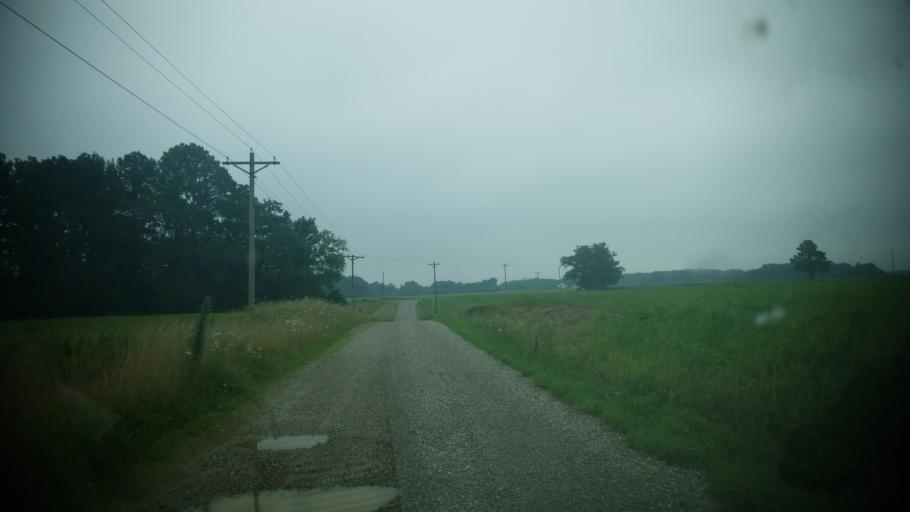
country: US
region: Illinois
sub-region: Clay County
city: Flora
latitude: 38.5882
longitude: -88.3672
